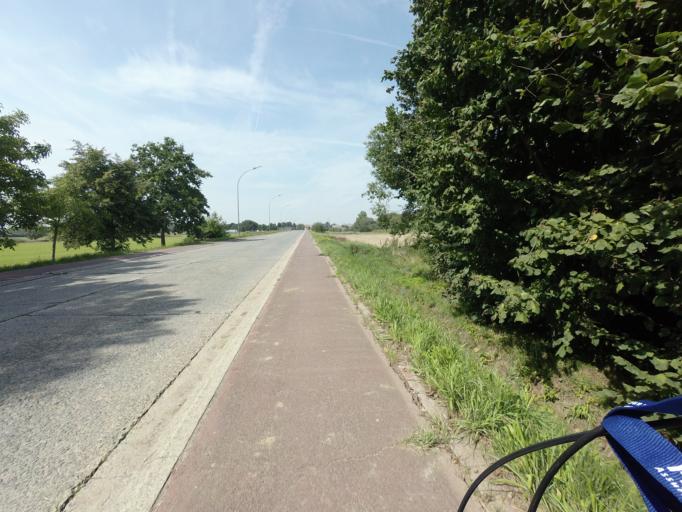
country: BE
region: Flanders
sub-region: Provincie Vlaams-Brabant
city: Zemst
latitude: 50.9680
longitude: 4.4834
